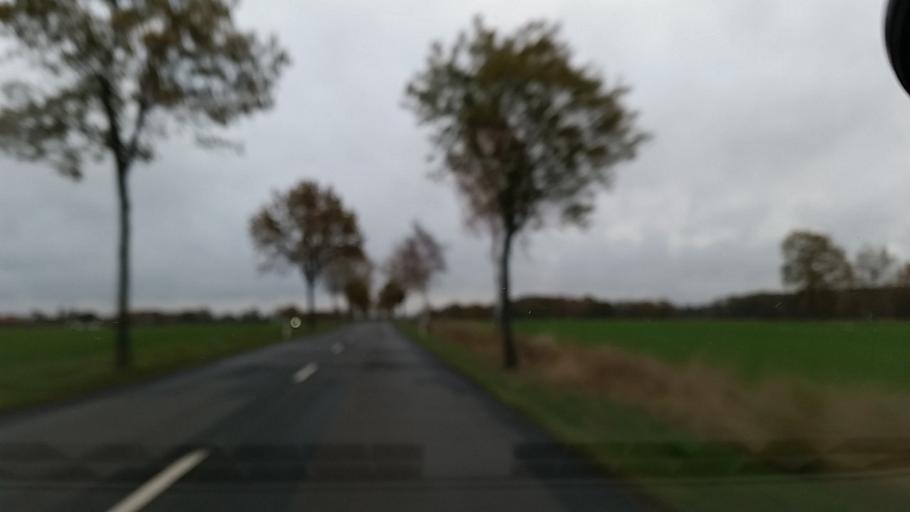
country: DE
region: Lower Saxony
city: Barwedel
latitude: 52.4994
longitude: 10.7869
